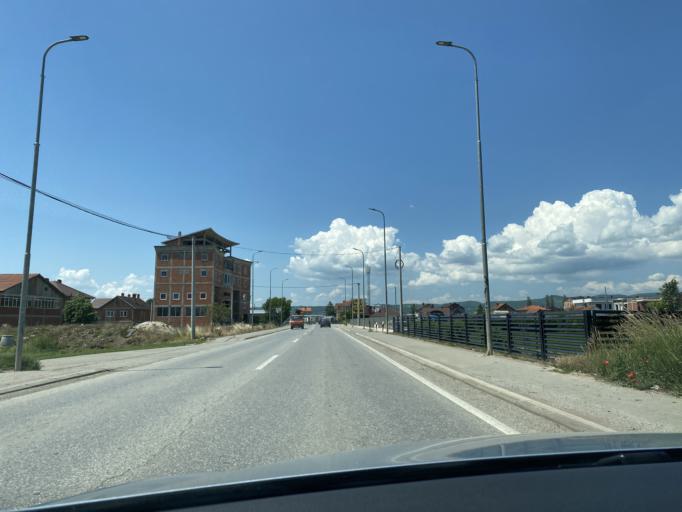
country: XK
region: Pristina
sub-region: Podujevo
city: Podujeva
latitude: 42.8976
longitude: 21.2012
